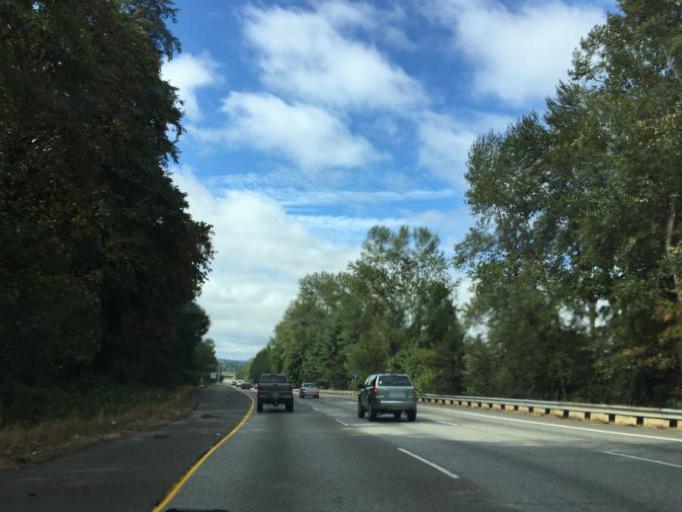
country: US
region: Washington
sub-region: Pierce County
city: DuPont
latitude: 47.0818
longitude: -122.6770
